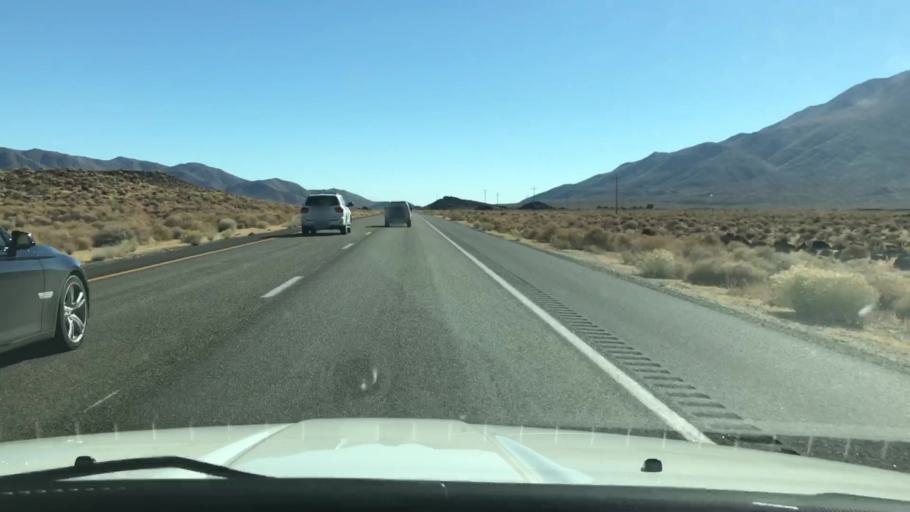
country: US
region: California
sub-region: Kern County
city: Inyokern
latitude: 35.9854
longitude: -117.9275
